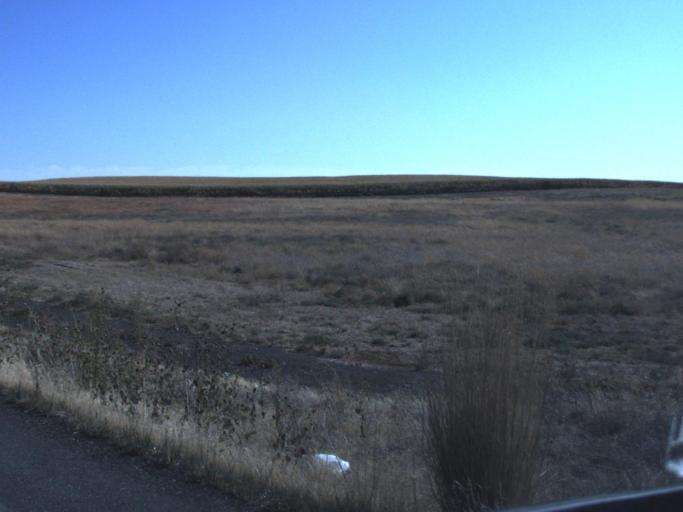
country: US
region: Washington
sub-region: Walla Walla County
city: Burbank
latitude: 46.2972
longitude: -118.6840
